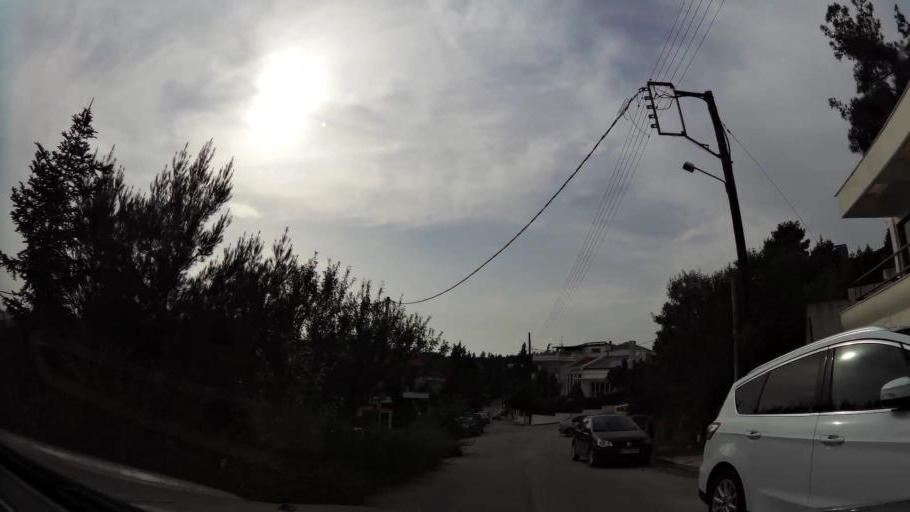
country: GR
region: Central Macedonia
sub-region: Nomos Thessalonikis
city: Oraiokastro
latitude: 40.7326
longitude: 22.9231
